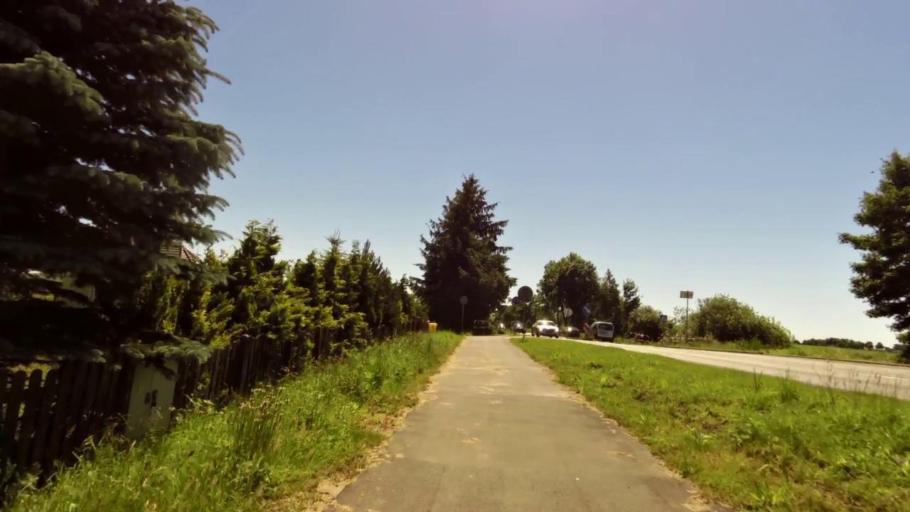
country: PL
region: West Pomeranian Voivodeship
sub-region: Powiat kolobrzeski
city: Kolobrzeg
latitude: 54.1360
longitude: 15.5591
